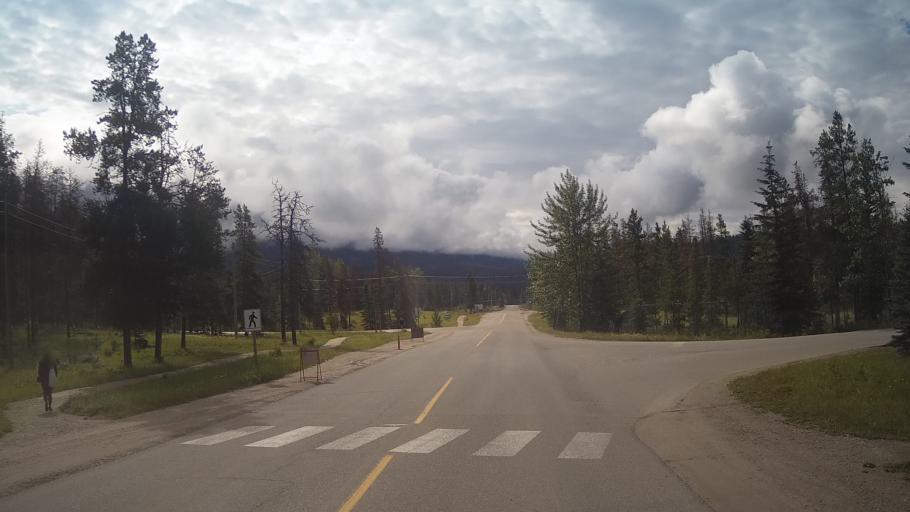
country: CA
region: Alberta
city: Jasper Park Lodge
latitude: 52.8717
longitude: -118.0801
